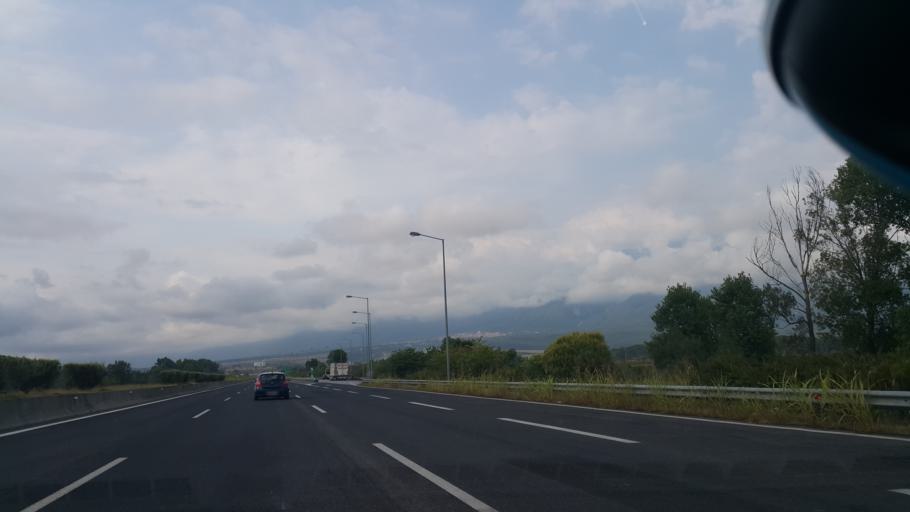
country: GR
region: Central Macedonia
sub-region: Nomos Pierias
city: Dion
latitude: 40.1616
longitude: 22.5447
